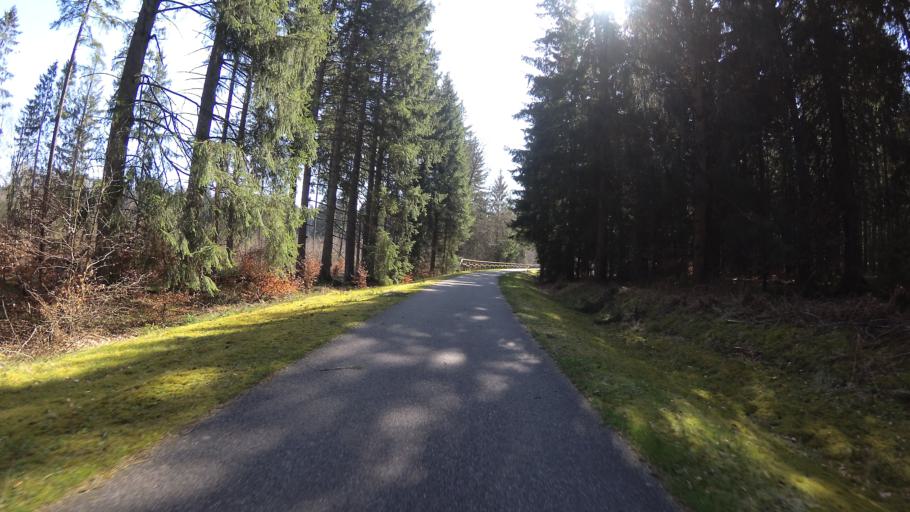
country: DE
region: Rheinland-Pfalz
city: Reinsfeld
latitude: 49.6598
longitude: 6.8553
